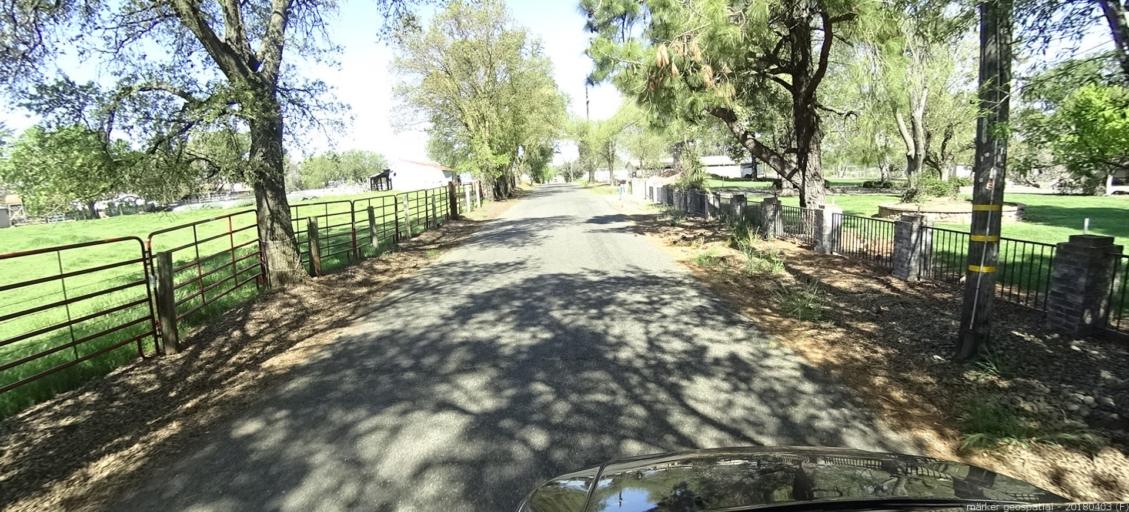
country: US
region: California
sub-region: Sacramento County
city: Wilton
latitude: 38.4287
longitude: -121.2127
